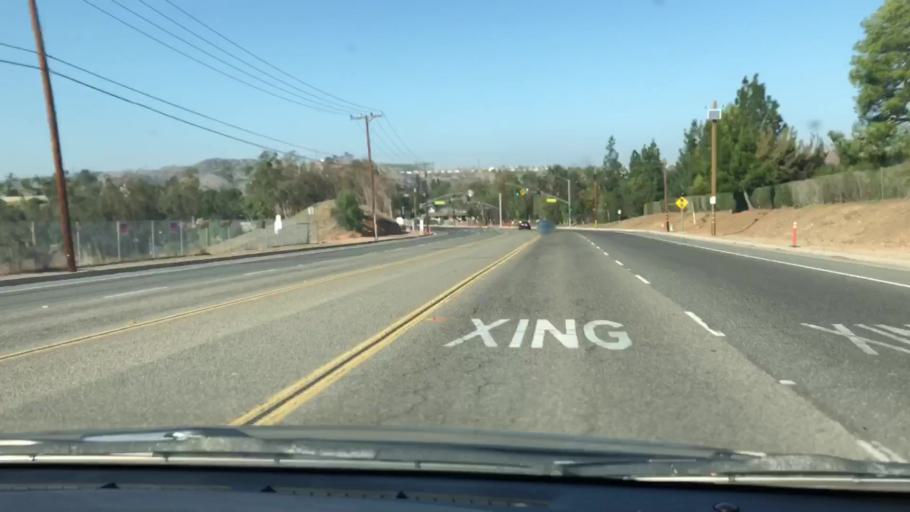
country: US
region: California
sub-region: Orange County
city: Villa Park
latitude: 33.8084
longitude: -117.7702
